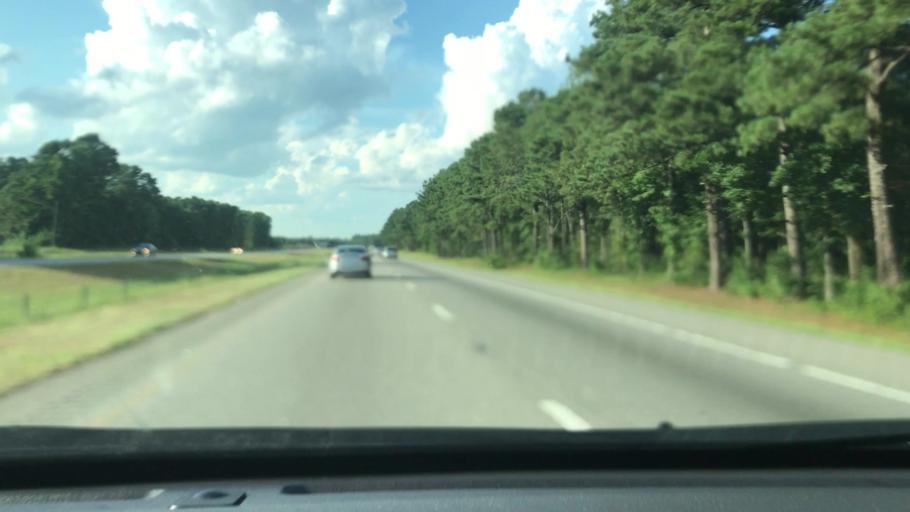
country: US
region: North Carolina
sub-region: Robeson County
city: Saint Pauls
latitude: 34.7829
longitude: -78.9950
